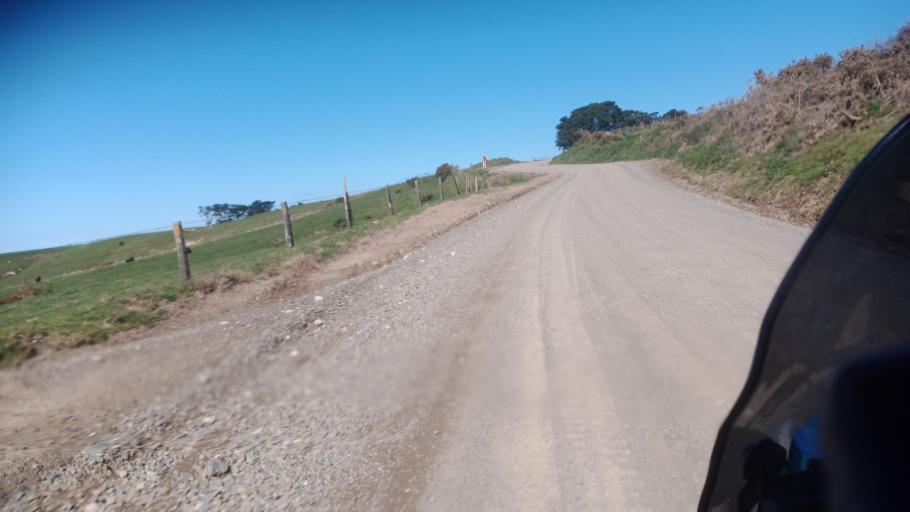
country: NZ
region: Gisborne
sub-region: Gisborne District
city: Gisborne
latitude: -39.1148
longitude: 177.9625
